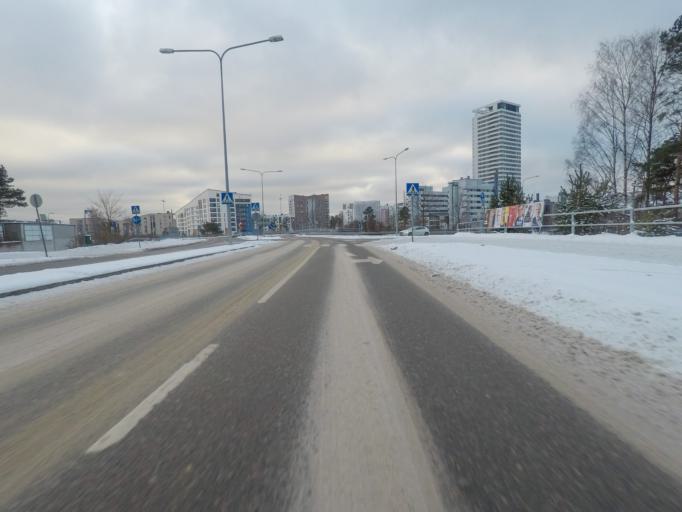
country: FI
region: Uusimaa
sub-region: Helsinki
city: Vantaa
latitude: 60.2083
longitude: 25.1485
